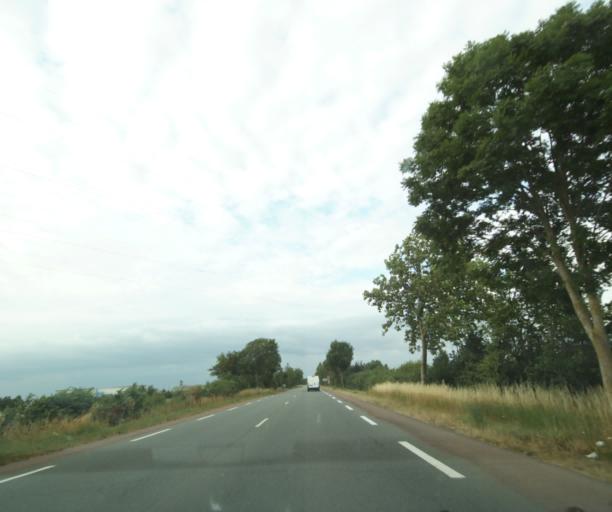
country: FR
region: Poitou-Charentes
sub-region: Departement de la Charente-Maritime
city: Marans
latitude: 46.2808
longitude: -0.9963
